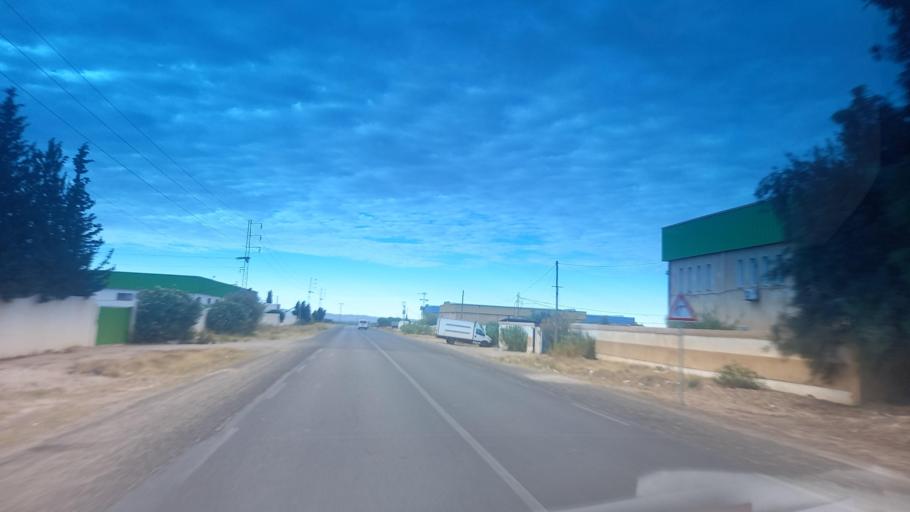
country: TN
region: Al Qasrayn
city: Sbiba
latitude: 35.2850
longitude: 9.0932
